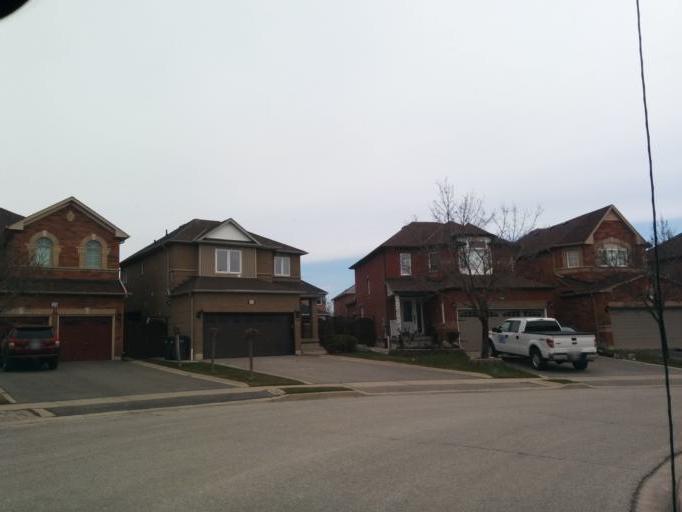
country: CA
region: Ontario
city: Brampton
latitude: 43.7301
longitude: -79.8243
